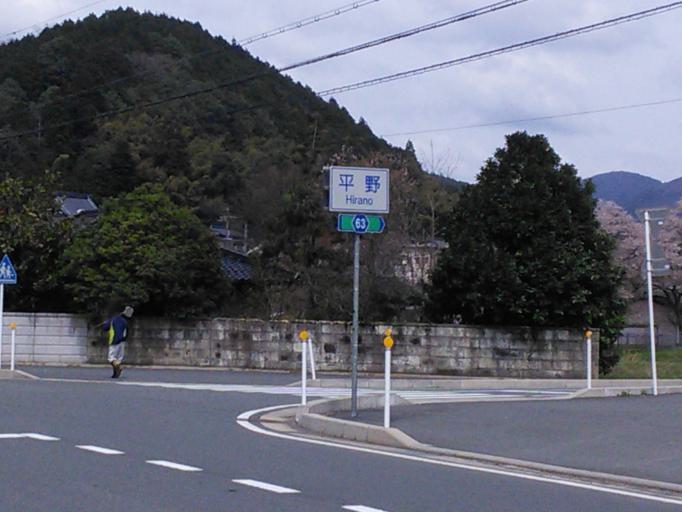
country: JP
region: Kyoto
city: Fukuchiyama
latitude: 35.3490
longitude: 134.9449
